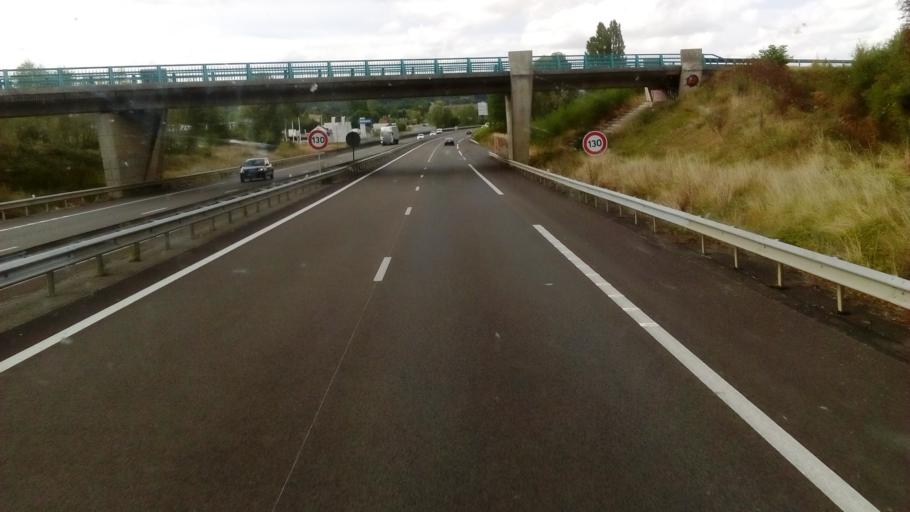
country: FR
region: Bourgogne
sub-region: Departement de la Nievre
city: Varennes-Vauzelles
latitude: 47.0433
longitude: 3.1367
